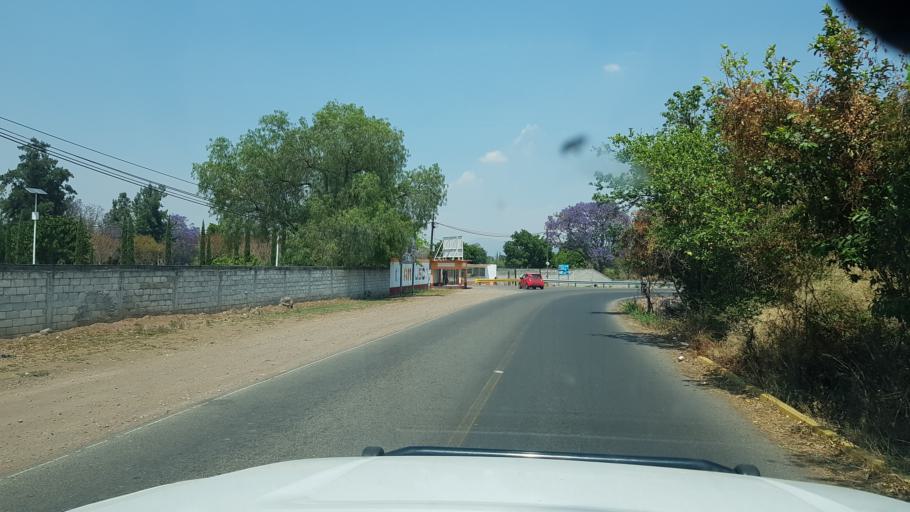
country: MX
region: Puebla
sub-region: Huaquechula
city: Cacaloxuchitl
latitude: 18.7926
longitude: -98.4658
